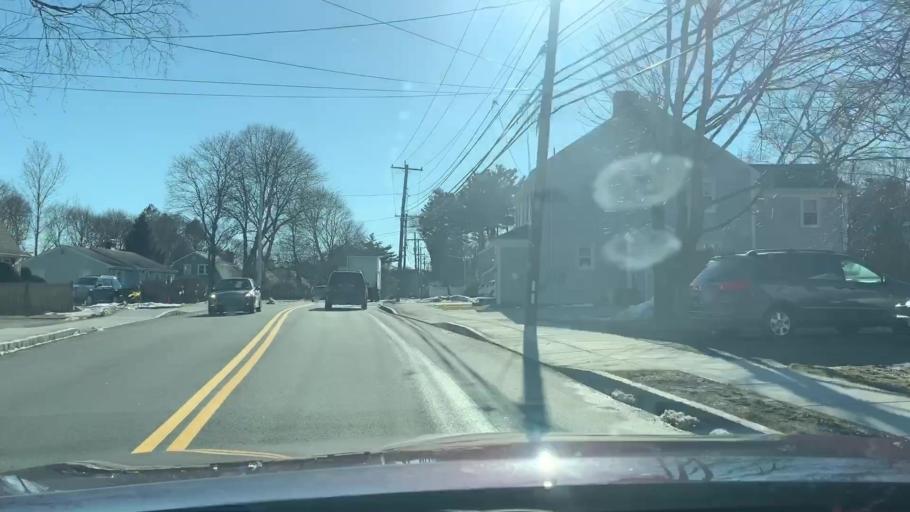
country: US
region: Massachusetts
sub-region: Essex County
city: Beverly Cove
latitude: 42.5698
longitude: -70.8588
